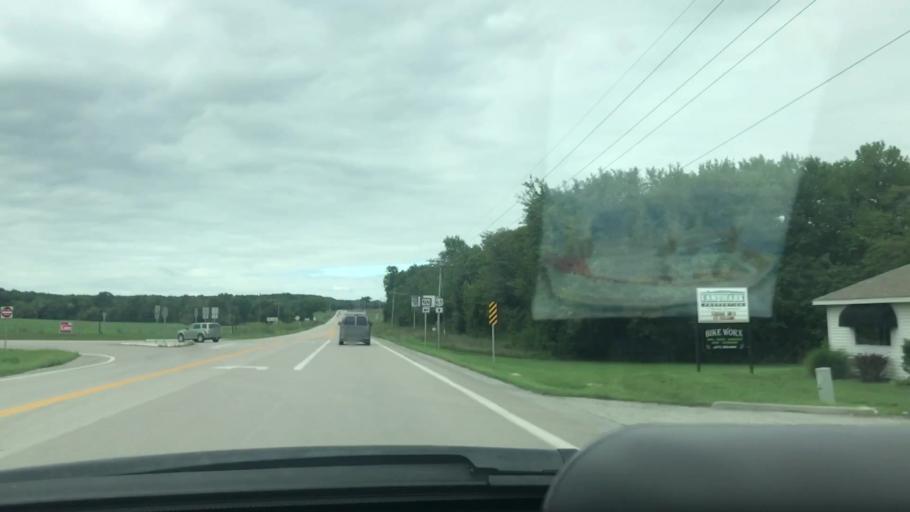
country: US
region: Missouri
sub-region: Hickory County
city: Hermitage
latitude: 37.8601
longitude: -93.1772
